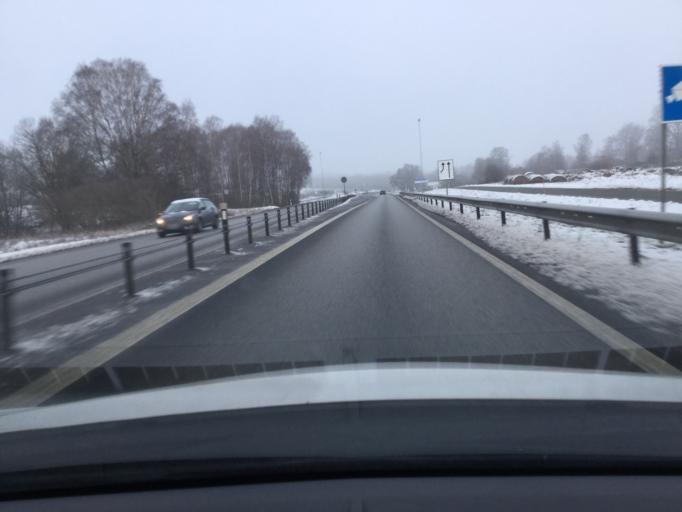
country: SE
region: Skane
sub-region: Kristianstads Kommun
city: Onnestad
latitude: 56.0385
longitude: 14.0437
